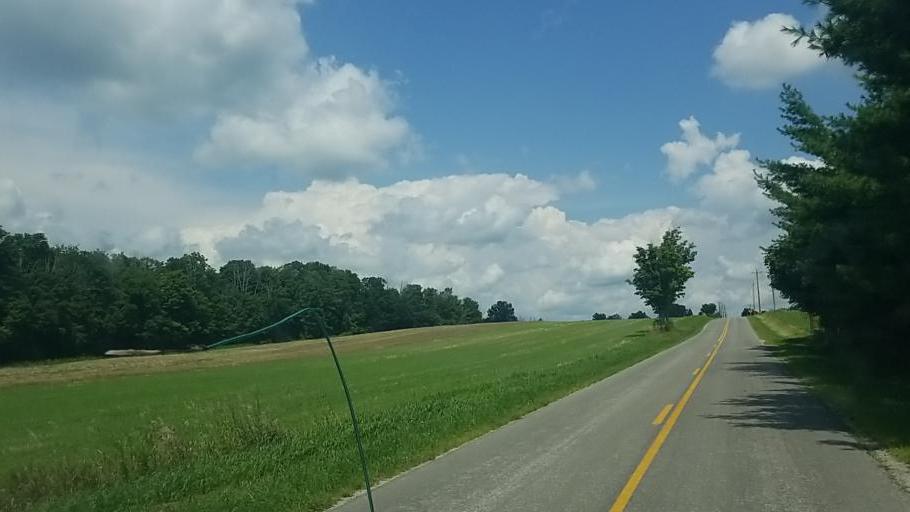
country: US
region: Ohio
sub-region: Medina County
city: Lodi
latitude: 41.0226
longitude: -82.0545
